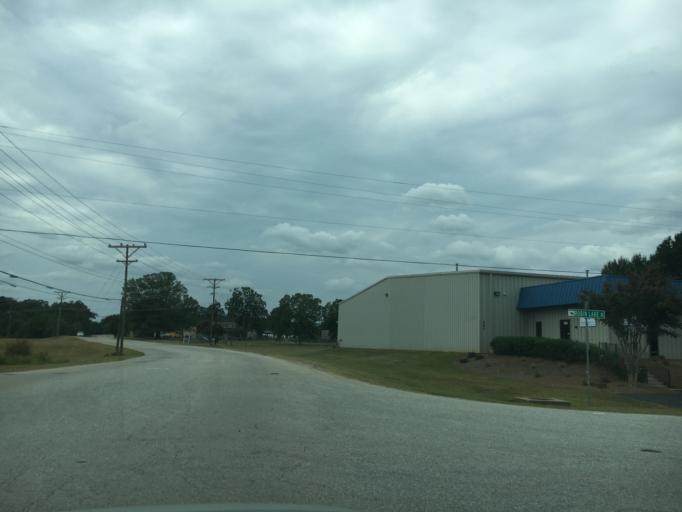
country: US
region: South Carolina
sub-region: Spartanburg County
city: Duncan
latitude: 34.9050
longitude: -82.1569
